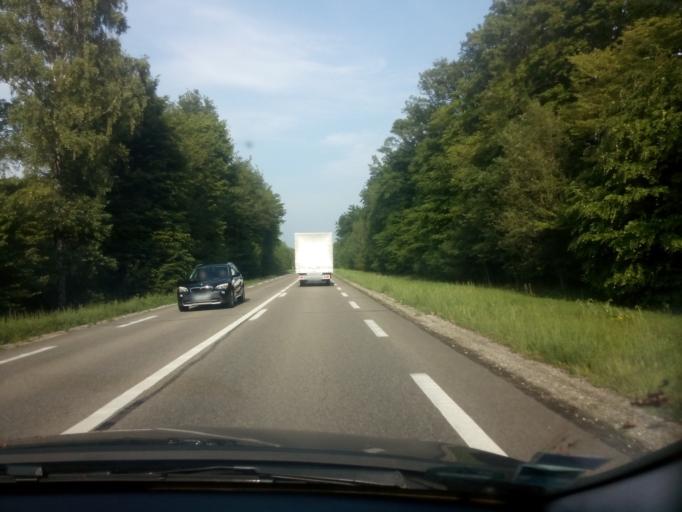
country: FR
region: Alsace
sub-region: Departement du Bas-Rhin
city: Kaltenhouse
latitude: 48.8335
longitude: 7.8599
